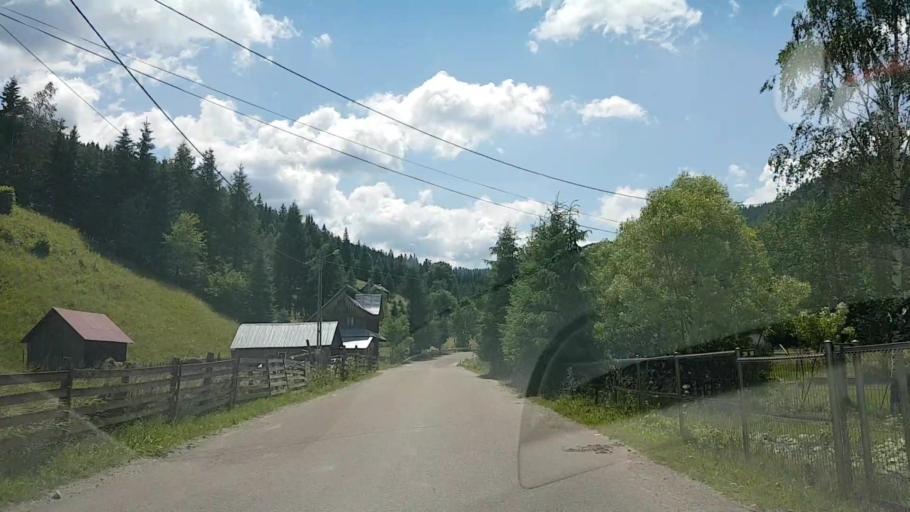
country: RO
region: Suceava
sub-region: Comuna Sadova
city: Sadova
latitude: 47.4843
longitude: 25.4909
